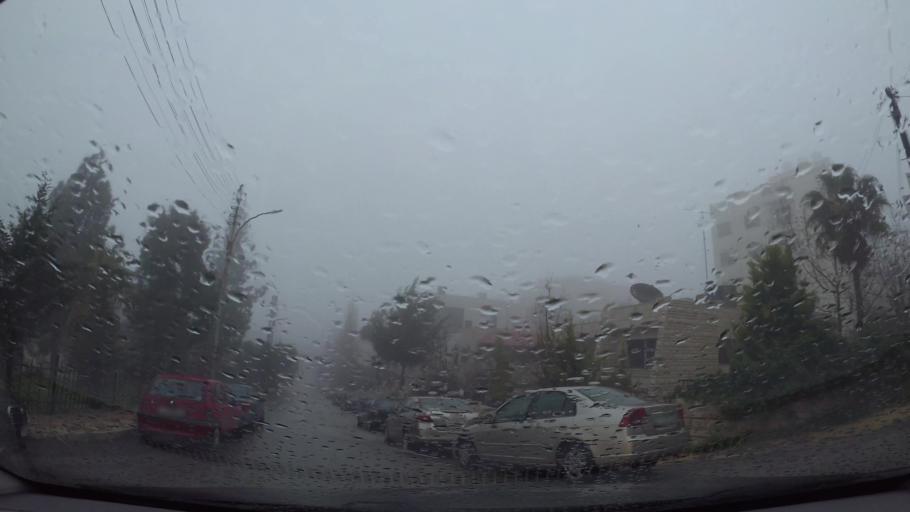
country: JO
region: Amman
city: Al Jubayhah
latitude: 32.0112
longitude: 35.8788
